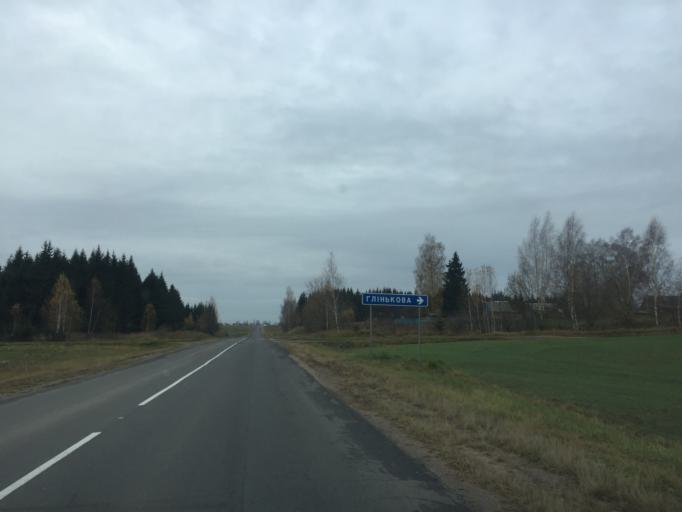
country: BY
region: Mogilev
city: Horki
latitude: 54.3134
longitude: 30.9548
